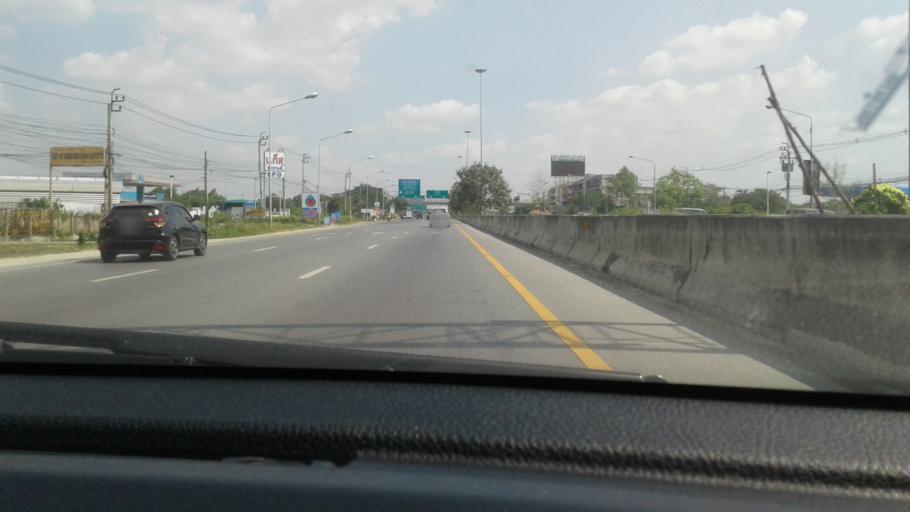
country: TH
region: Nonthaburi
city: Bang Bua Thong
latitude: 13.9491
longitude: 100.4493
